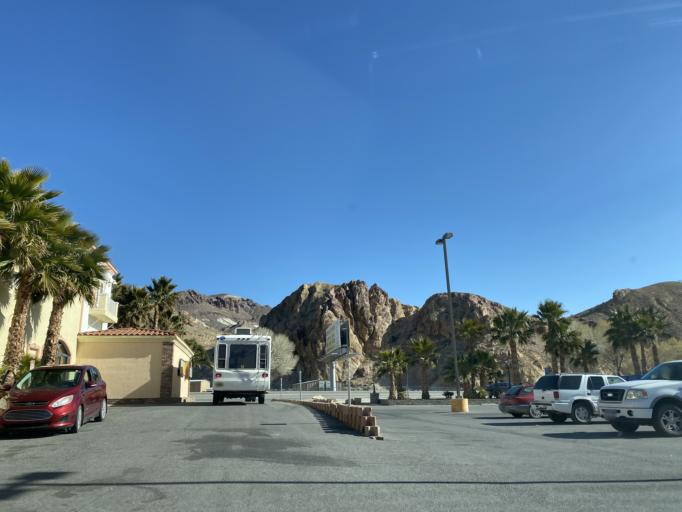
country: US
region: Nevada
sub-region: Nye County
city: Beatty
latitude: 36.9134
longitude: -116.7544
